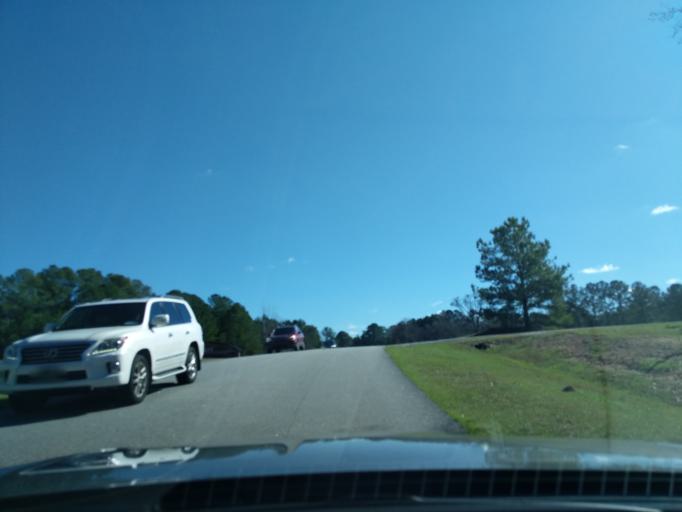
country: US
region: Georgia
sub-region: Columbia County
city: Evans
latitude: 33.5541
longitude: -82.1681
